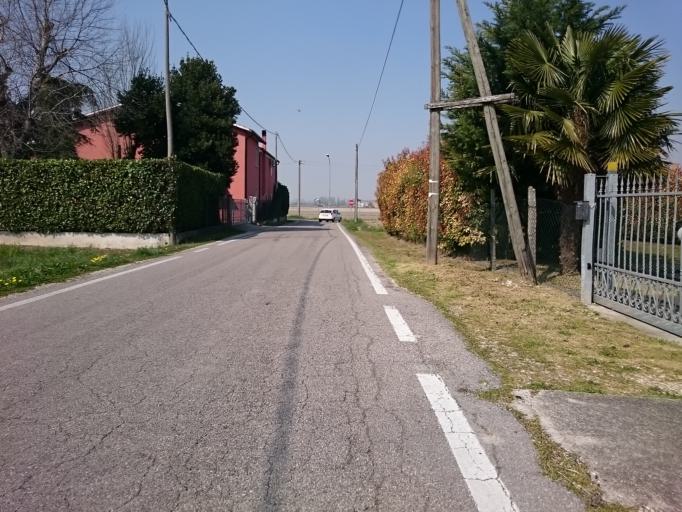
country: IT
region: Veneto
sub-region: Provincia di Padova
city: Villa Estense
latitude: 45.1850
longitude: 11.6704
